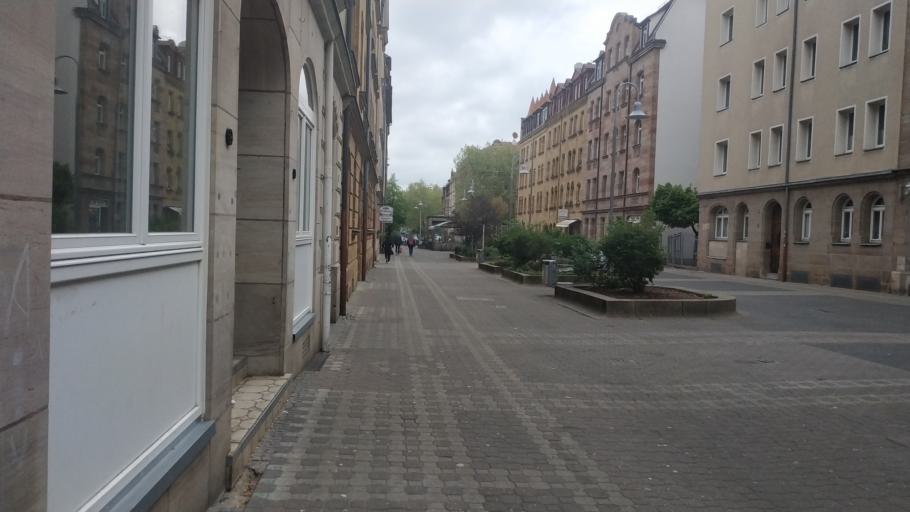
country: DE
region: Bavaria
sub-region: Regierungsbezirk Mittelfranken
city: Grossreuth bei Schweinau
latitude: 49.4387
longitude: 11.0499
